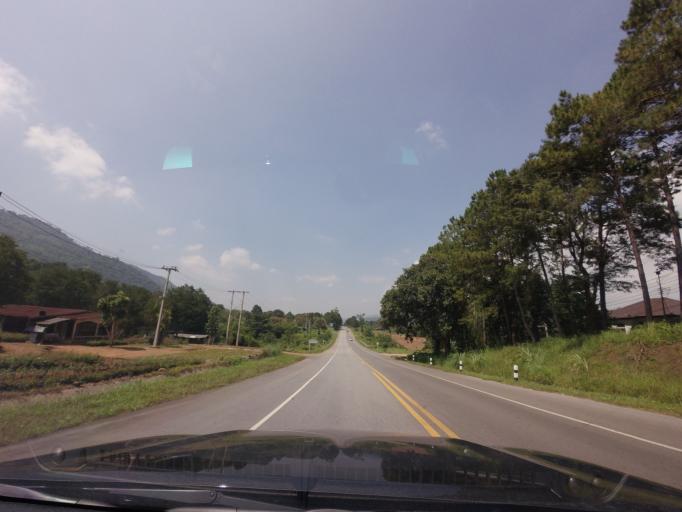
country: TH
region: Loei
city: Phu Ruea
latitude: 17.4593
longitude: 101.4126
